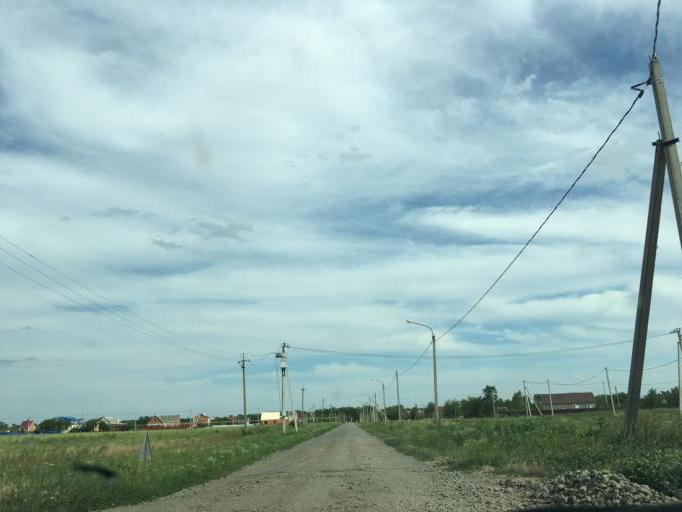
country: RU
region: Krasnodarskiy
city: Kushchevskaya
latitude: 46.5532
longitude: 39.6679
